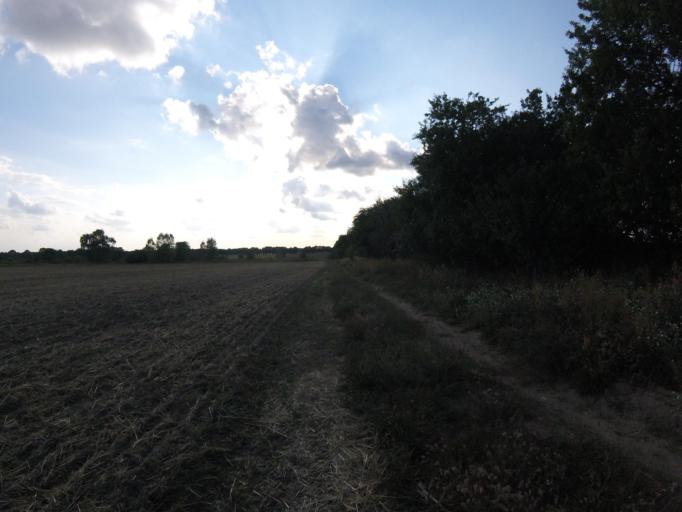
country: DE
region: Brandenburg
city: Mittenwalde
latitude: 52.3027
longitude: 13.5461
